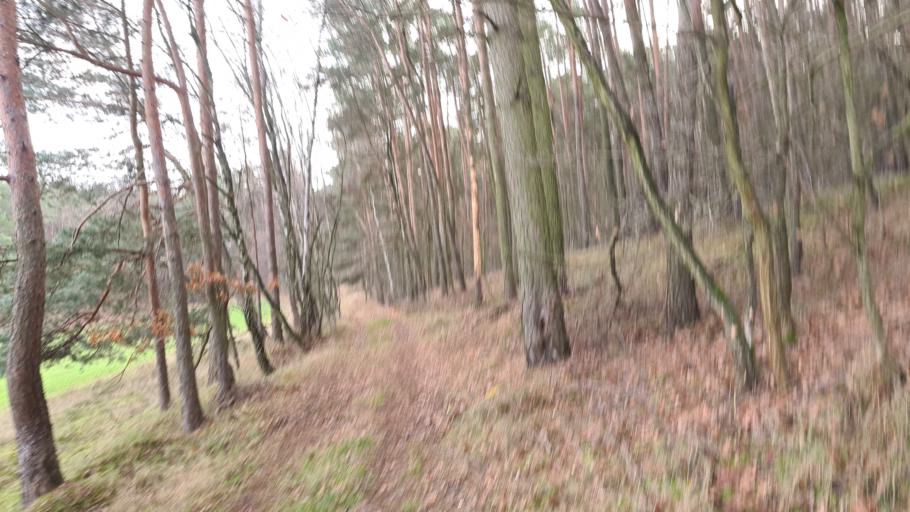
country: DE
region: Brandenburg
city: Groden
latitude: 51.3929
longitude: 13.5781
